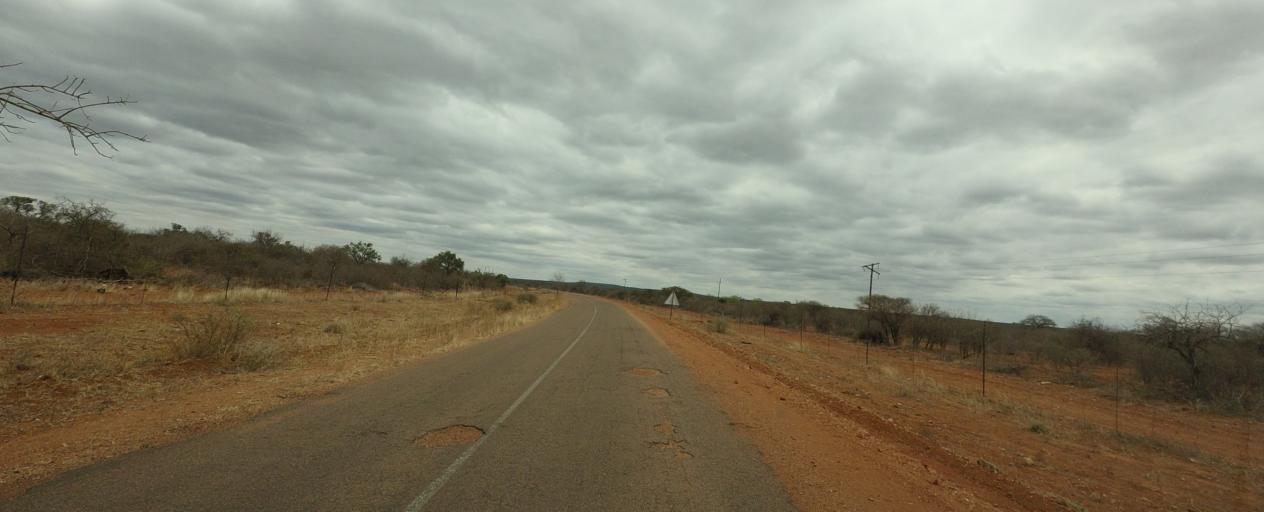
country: BW
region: Central
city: Mathathane
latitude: -22.7389
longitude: 28.4592
